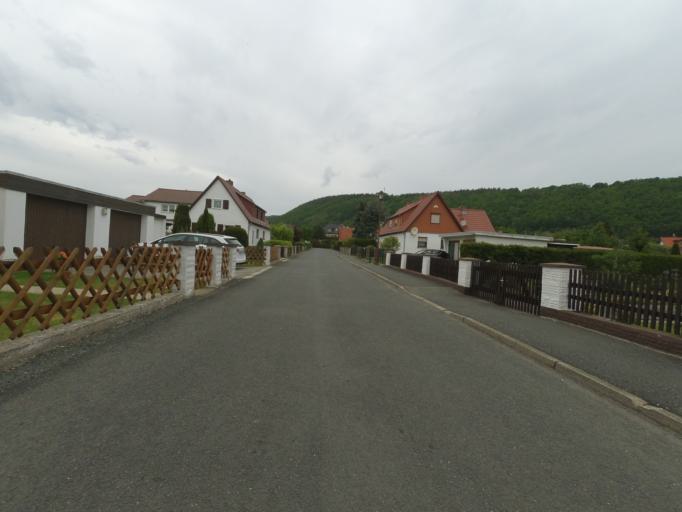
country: DE
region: Thuringia
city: Bad Blankenburg
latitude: 50.6844
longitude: 11.3137
